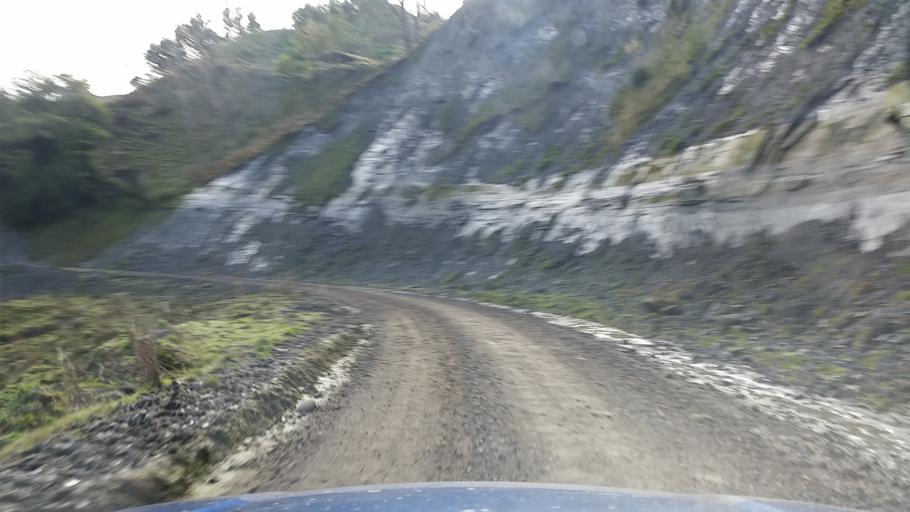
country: NZ
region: Taranaki
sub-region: New Plymouth District
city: Waitara
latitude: -39.1087
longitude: 174.8485
